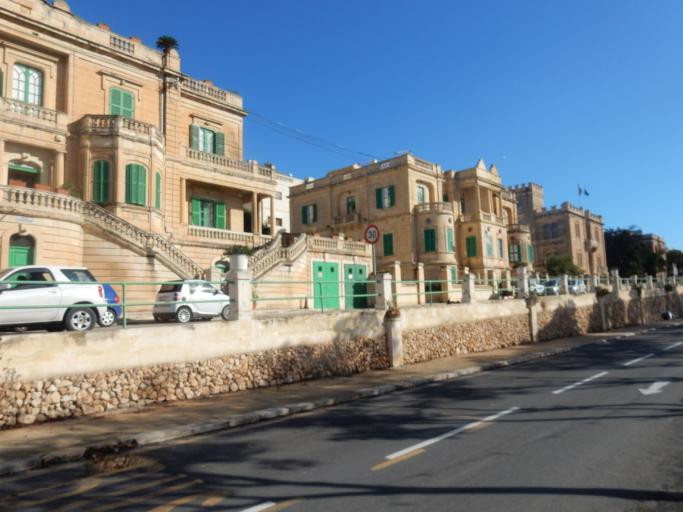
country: MT
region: Ta' Xbiex
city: Ta' Xbiex
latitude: 35.8979
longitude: 14.4971
